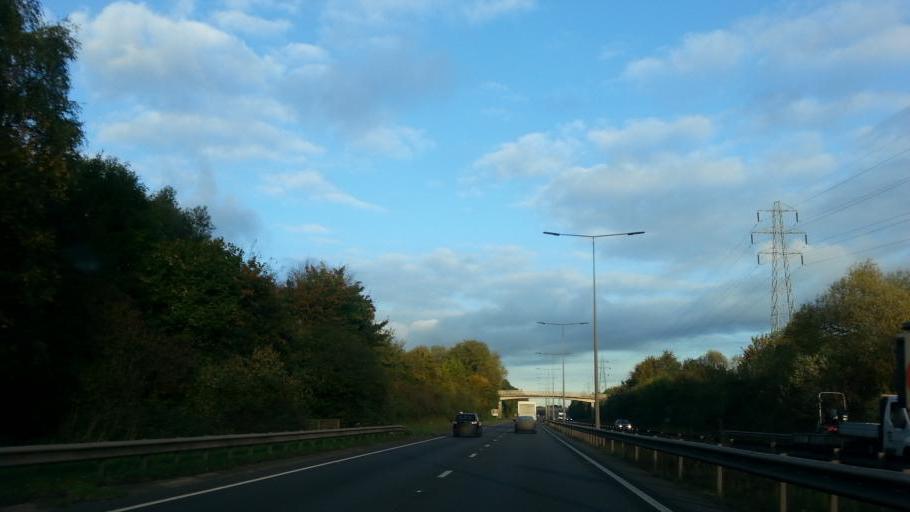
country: GB
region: England
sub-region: Staffordshire
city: Fazeley
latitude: 52.6127
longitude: -1.6608
